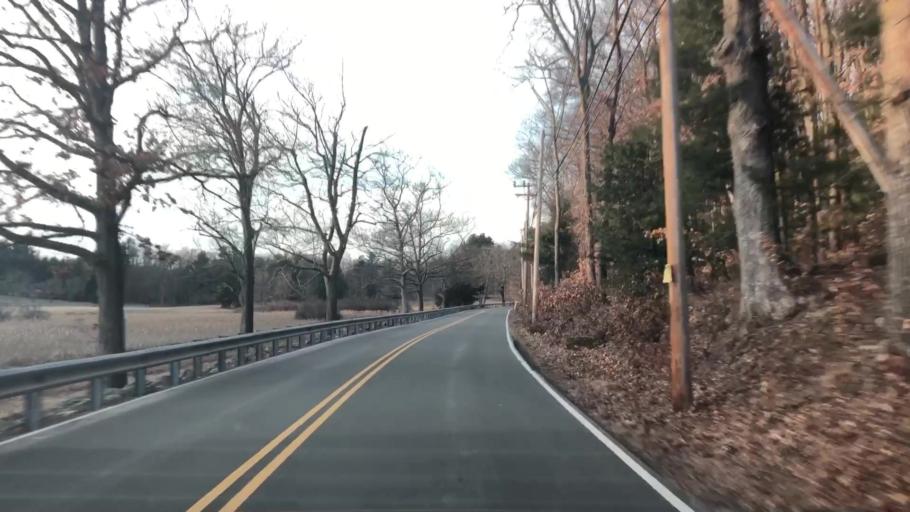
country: US
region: Massachusetts
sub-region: Essex County
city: North Andover
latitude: 42.7096
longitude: -71.0854
